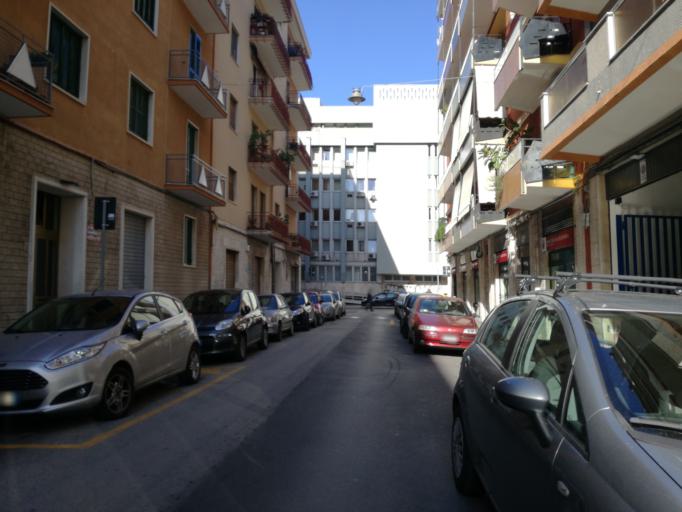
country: IT
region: Apulia
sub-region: Provincia di Bari
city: Bari
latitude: 41.1229
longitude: 16.8558
